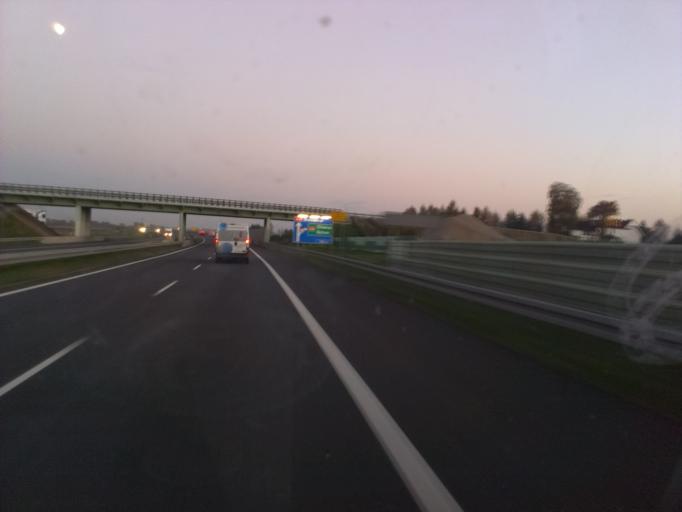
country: PL
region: Silesian Voivodeship
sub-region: Powiat gliwicki
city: Sosnicowice
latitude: 50.3515
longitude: 18.5275
